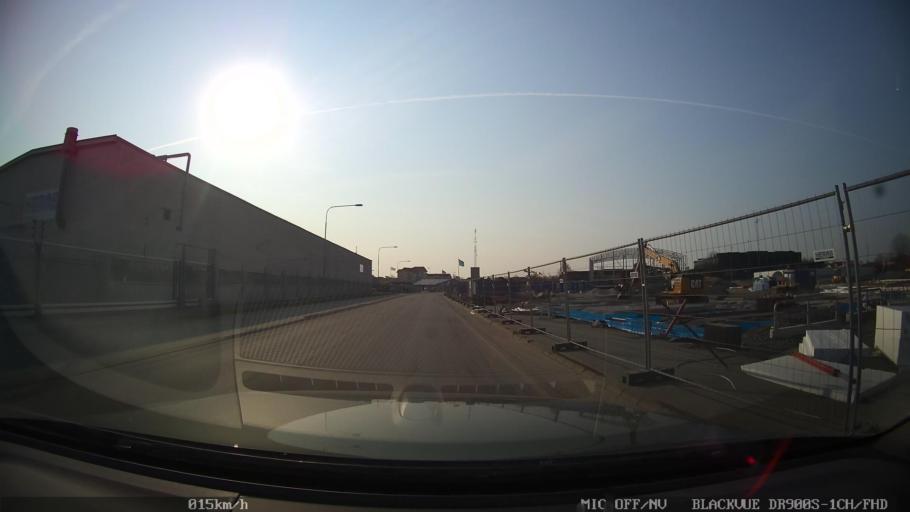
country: SE
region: Skane
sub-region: Ystads Kommun
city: Ystad
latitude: 55.4361
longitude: 13.8329
